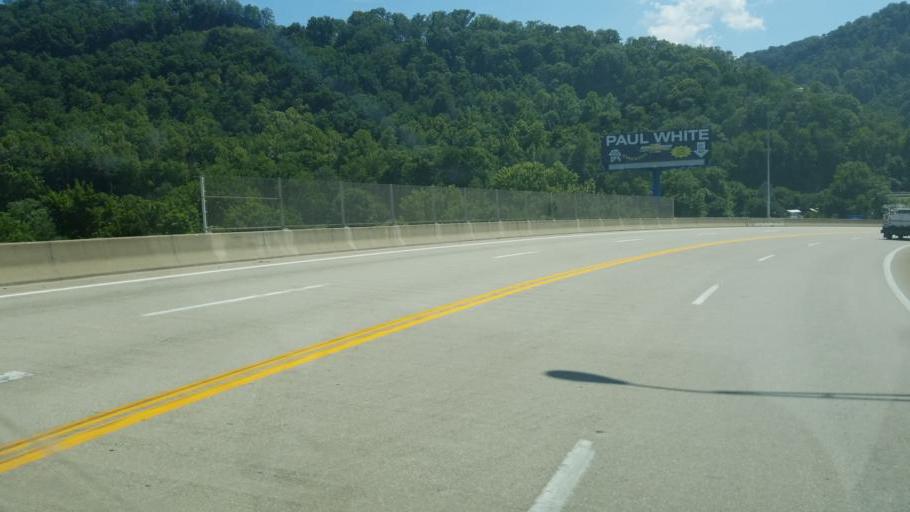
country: US
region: West Virginia
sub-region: Kanawha County
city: Chesapeake
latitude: 38.1957
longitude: -81.4969
